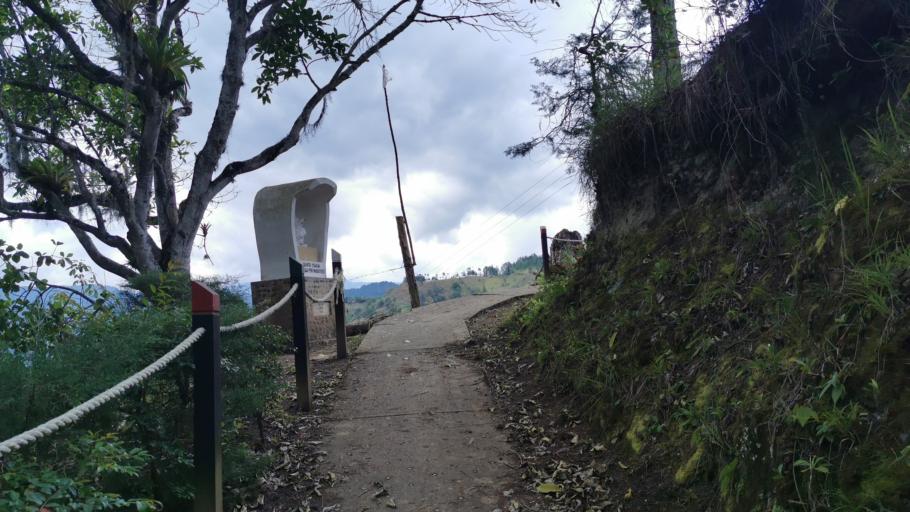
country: CO
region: Cundinamarca
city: Tenza
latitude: 5.0745
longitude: -73.4199
